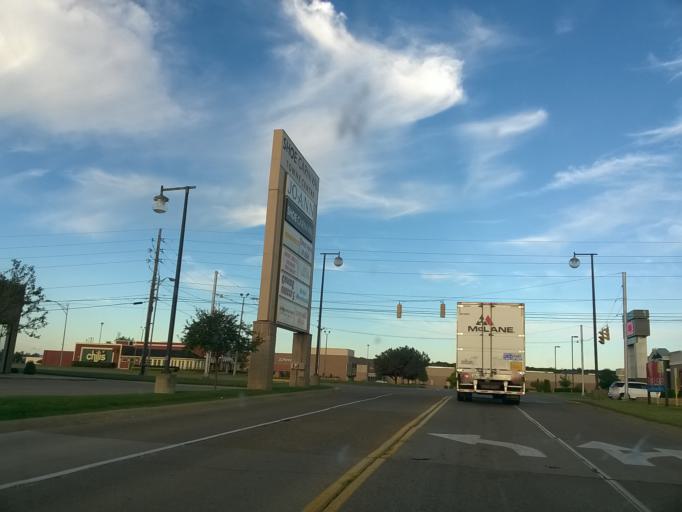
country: US
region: Indiana
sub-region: Vanderburgh County
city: Melody Hill
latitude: 37.9834
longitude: -87.4921
